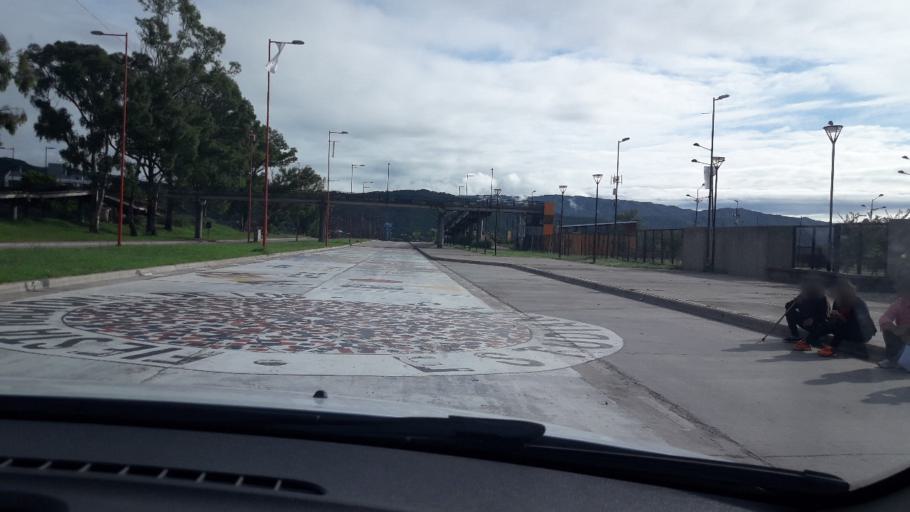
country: AR
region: Jujuy
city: San Salvador de Jujuy
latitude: -24.1826
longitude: -65.3311
